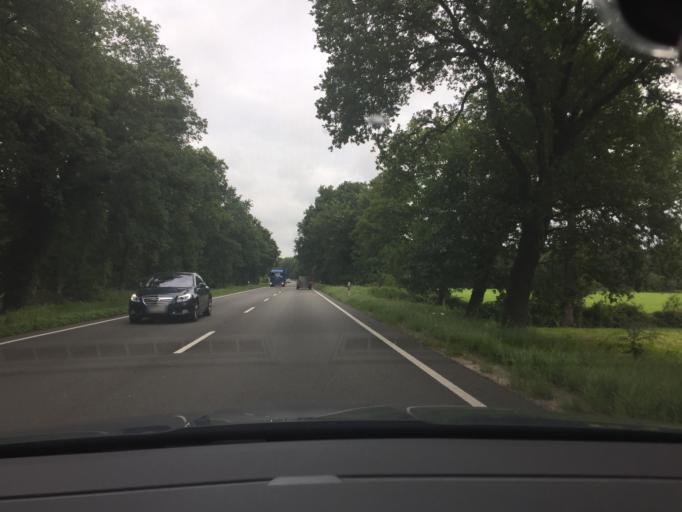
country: DE
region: Lower Saxony
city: Aurich
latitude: 53.4490
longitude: 7.5052
